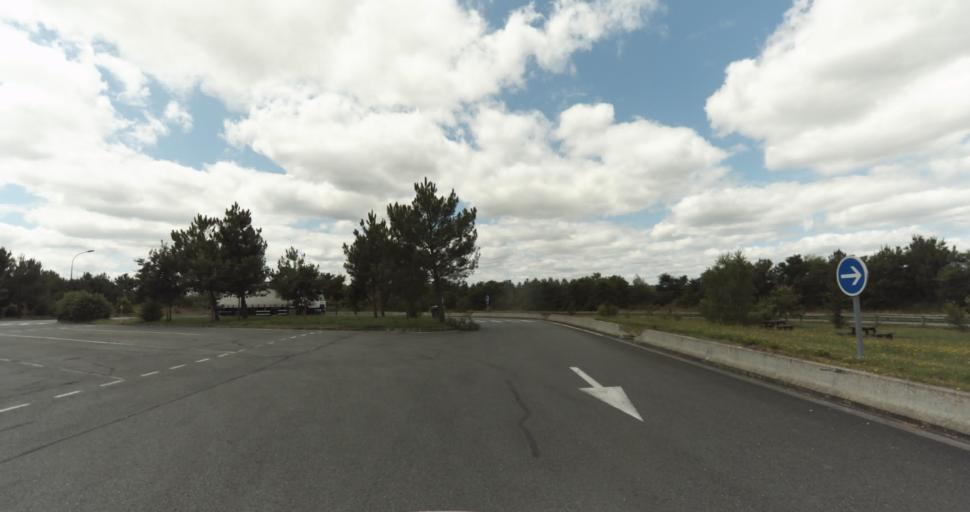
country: FR
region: Aquitaine
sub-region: Departement de la Gironde
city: Bazas
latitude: 44.4459
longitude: -0.2443
